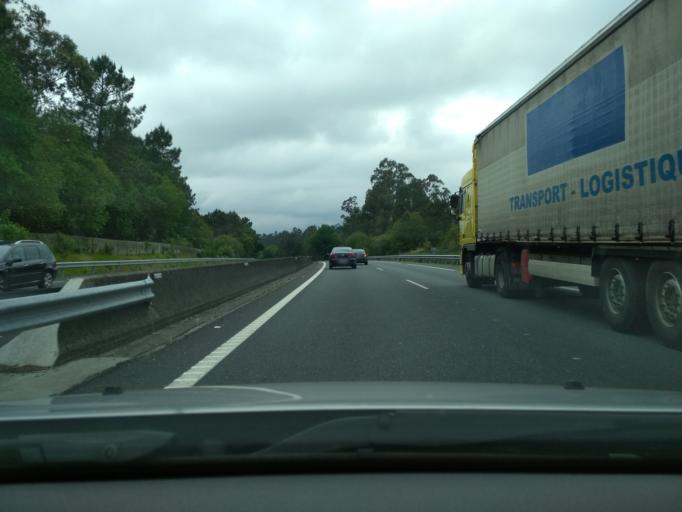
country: ES
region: Galicia
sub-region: Provincia da Coruna
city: Santiago de Compostela
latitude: 42.8086
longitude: -8.5966
